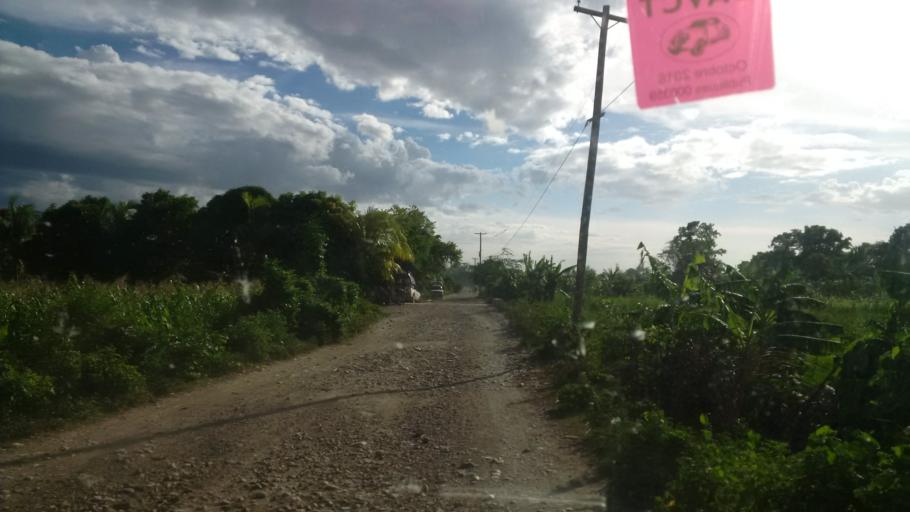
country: HT
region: Ouest
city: Thomazeau
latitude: 18.6548
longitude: -72.0837
